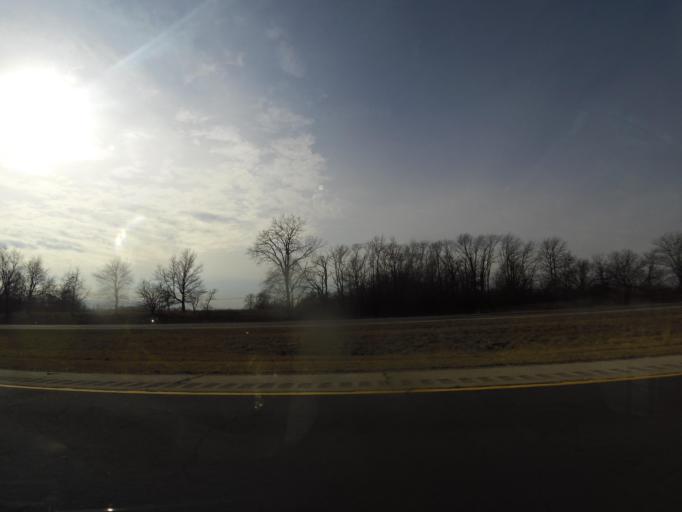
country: US
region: Illinois
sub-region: Macon County
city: Decatur
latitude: 39.7917
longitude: -88.9943
